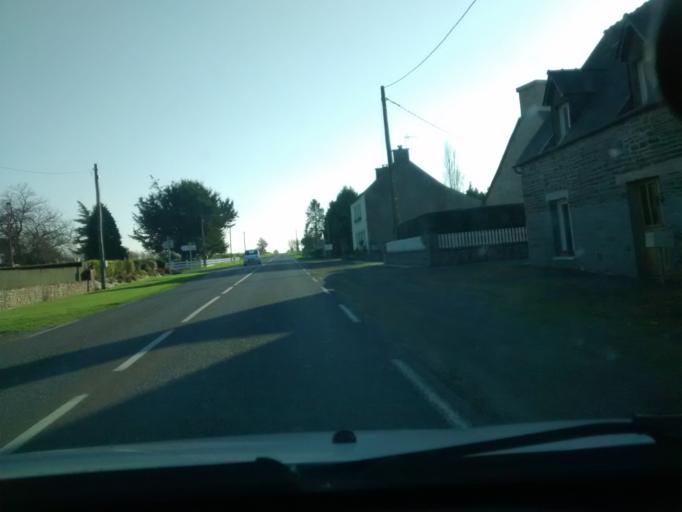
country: FR
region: Lower Normandy
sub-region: Departement de la Manche
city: Pontorson
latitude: 48.5258
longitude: -1.4845
